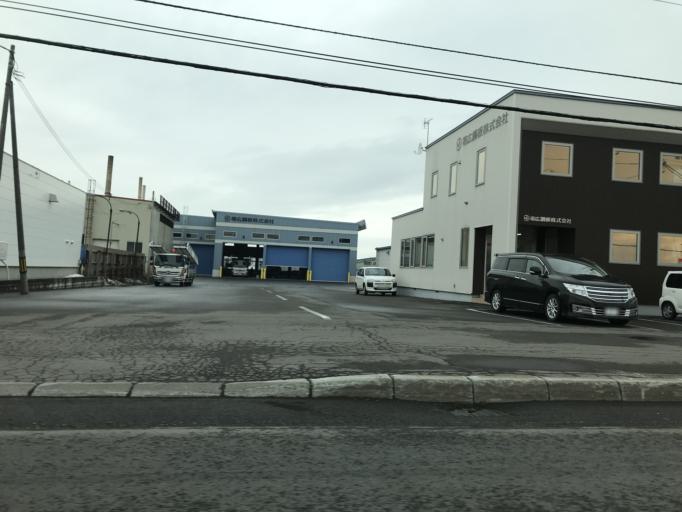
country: JP
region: Hokkaido
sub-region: Asahikawa-shi
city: Asahikawa
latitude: 43.8172
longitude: 142.4054
